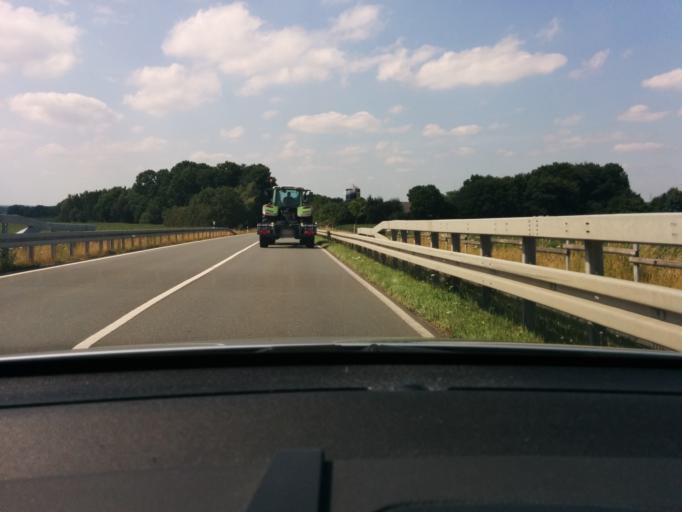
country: DE
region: North Rhine-Westphalia
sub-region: Regierungsbezirk Munster
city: Wettringen
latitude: 52.1701
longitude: 7.2906
